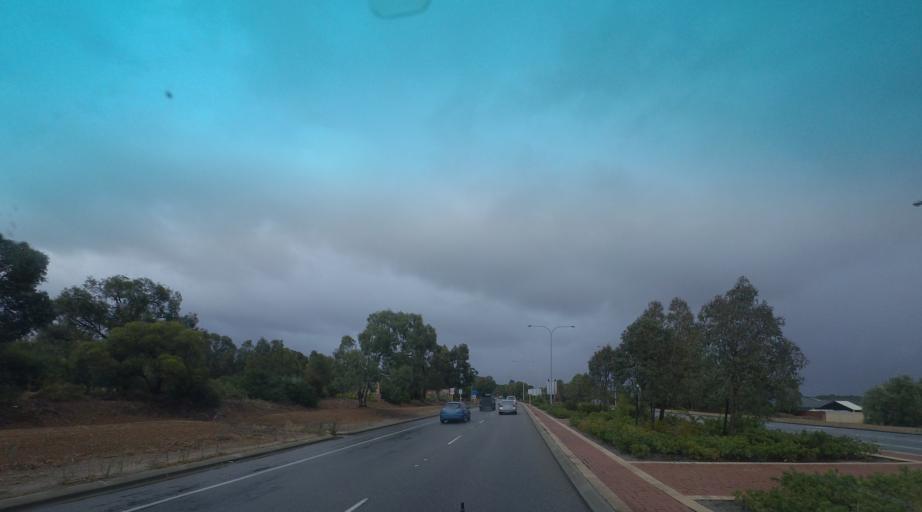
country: AU
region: Western Australia
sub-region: Serpentine-Jarrahdale
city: Byford
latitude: -32.2052
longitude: 116.0118
